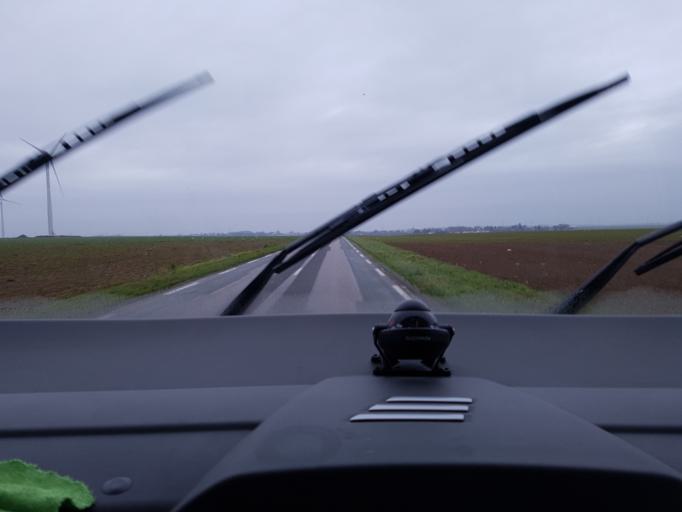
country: FR
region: Haute-Normandie
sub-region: Departement de l'Eure
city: Beaumont-le-Roger
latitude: 49.1007
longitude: 0.8200
